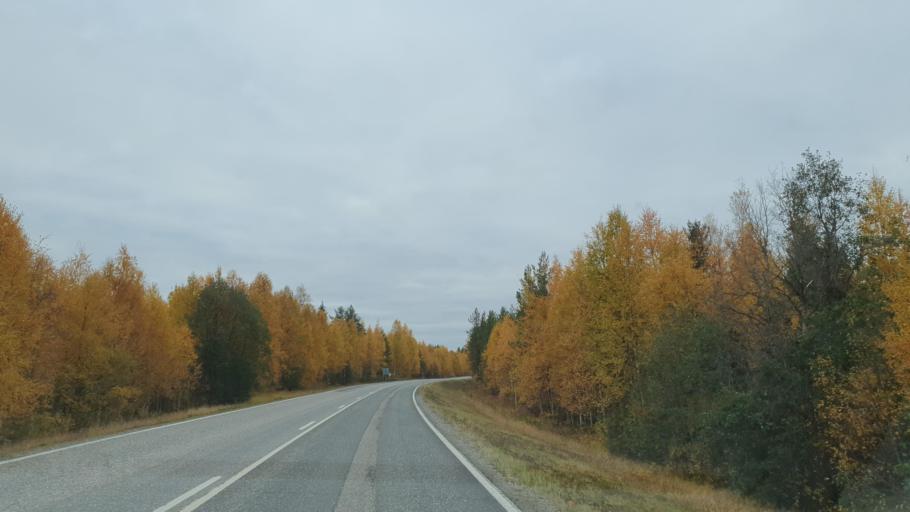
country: FI
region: Lapland
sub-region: Tunturi-Lappi
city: Kittilae
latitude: 67.3111
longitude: 24.9113
